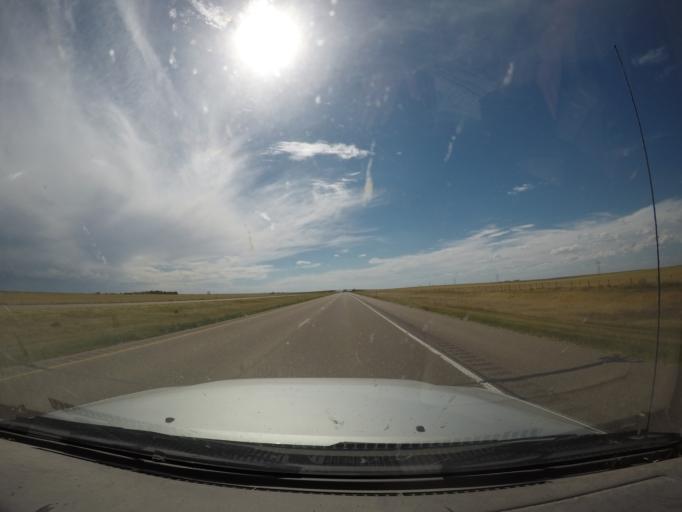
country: US
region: Nebraska
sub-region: Deuel County
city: Chappell
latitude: 41.0498
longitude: -102.3672
